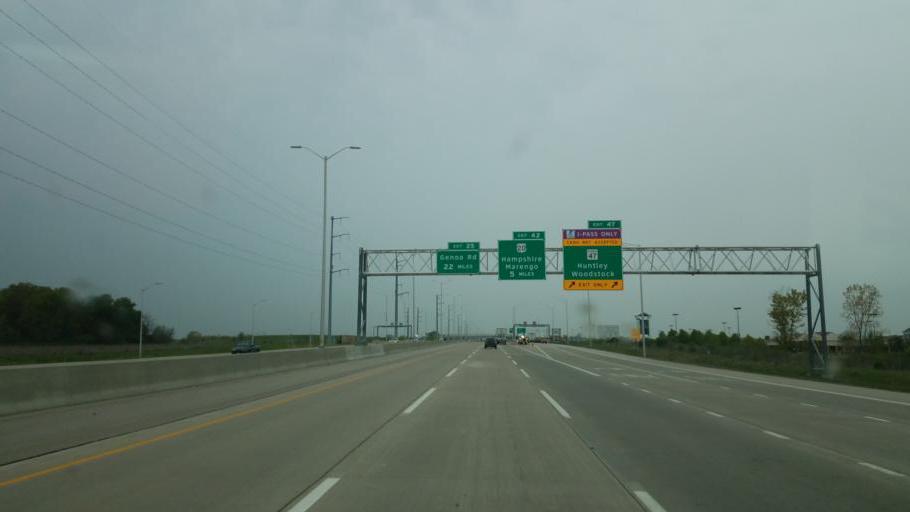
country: US
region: Illinois
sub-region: McHenry County
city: Huntley
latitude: 42.1182
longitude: -88.4242
